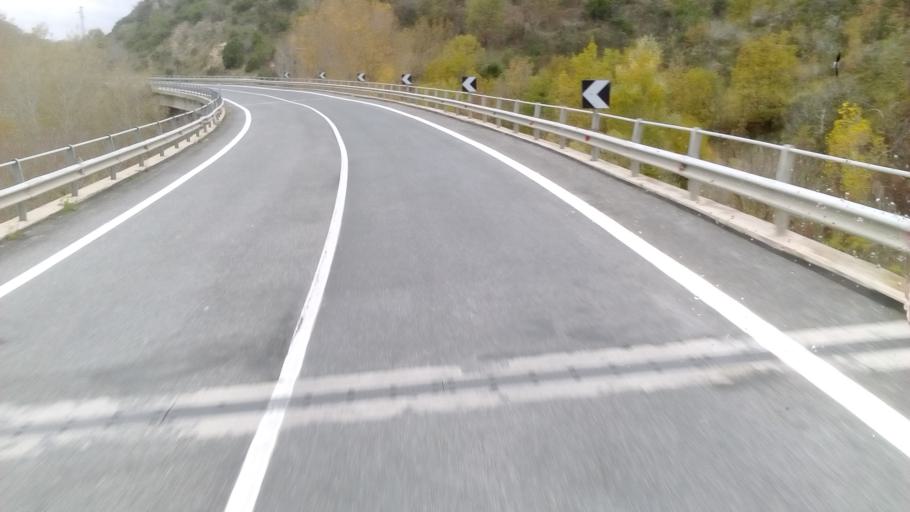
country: IT
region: Molise
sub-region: Provincia di Campobasso
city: Trivento
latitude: 41.7905
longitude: 14.5325
